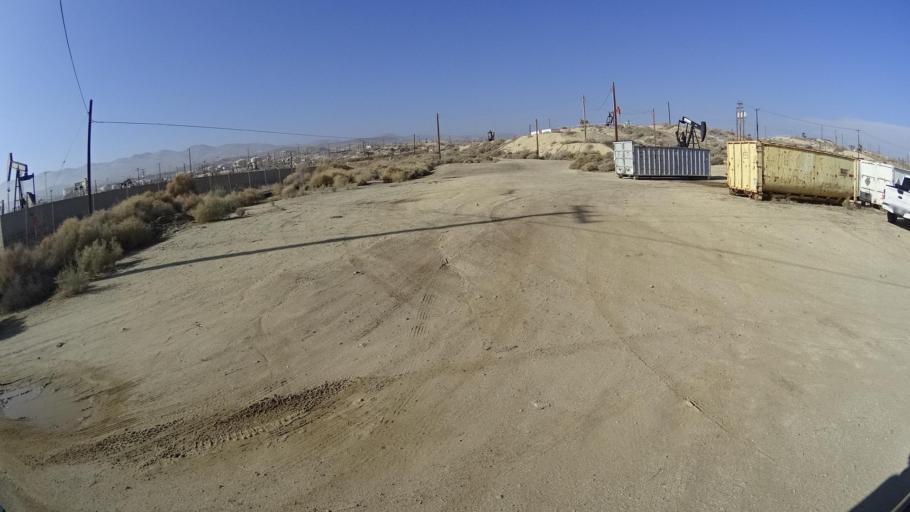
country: US
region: California
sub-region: Kern County
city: Taft Heights
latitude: 35.2168
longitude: -119.5983
